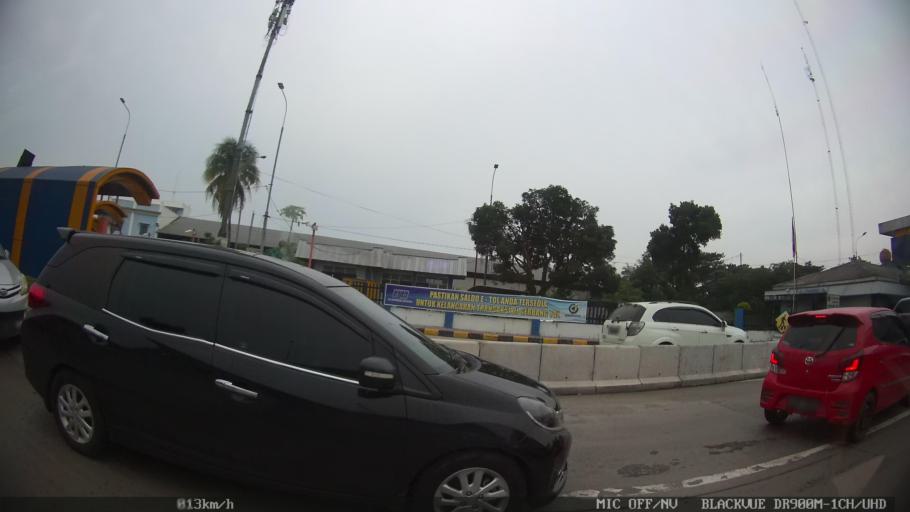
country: ID
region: North Sumatra
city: Deli Tua
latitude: 3.5380
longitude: 98.7221
